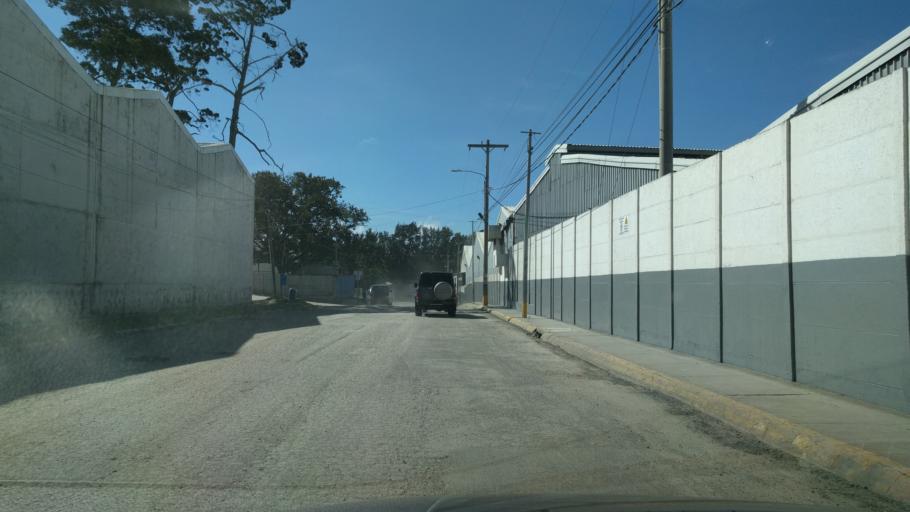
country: GT
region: Guatemala
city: Villa Nueva
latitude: 14.5808
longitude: -90.5650
